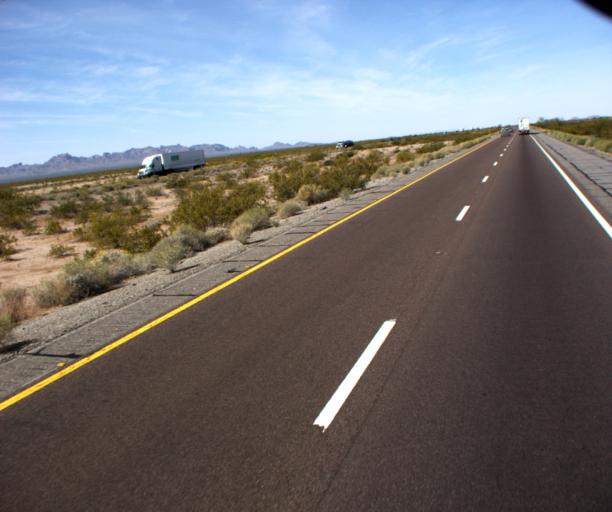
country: US
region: Arizona
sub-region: La Paz County
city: Salome
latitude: 33.5534
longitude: -113.2481
